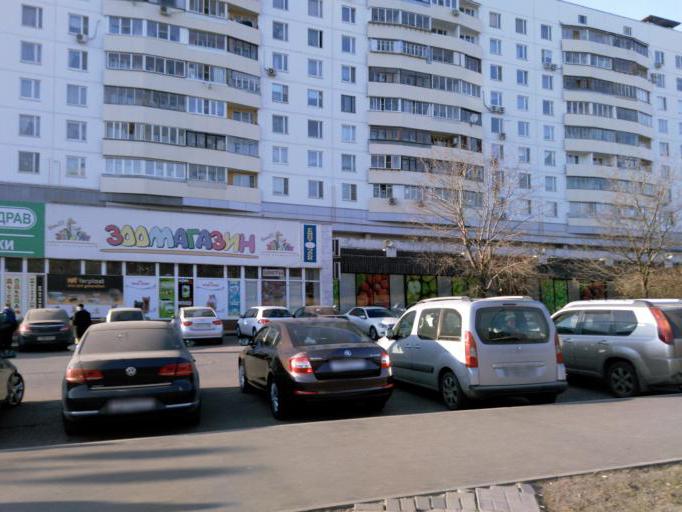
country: RU
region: Moscow
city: Troparevo
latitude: 55.6550
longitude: 37.4854
